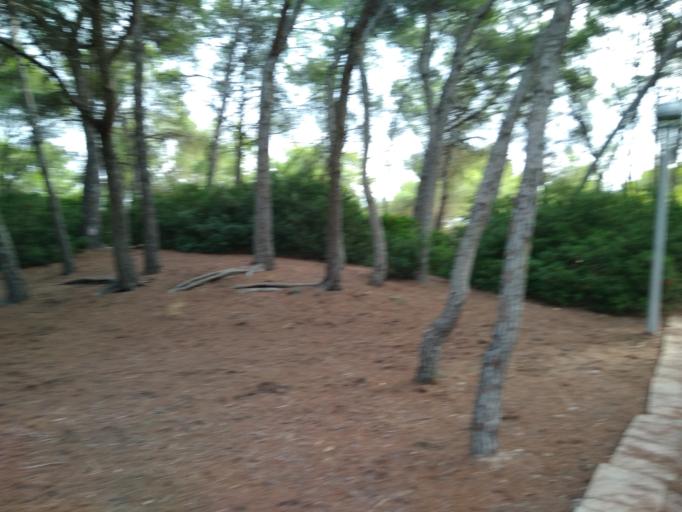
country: ES
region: Balearic Islands
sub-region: Illes Balears
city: s'Arenal
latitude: 39.5272
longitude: 2.7395
